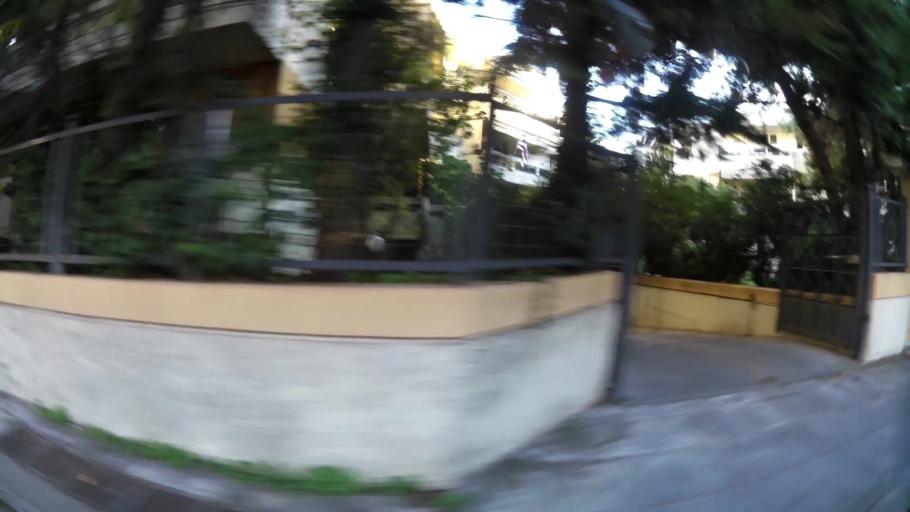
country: GR
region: Attica
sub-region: Nomarchia Athinas
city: Kifisia
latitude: 38.0708
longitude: 23.8025
